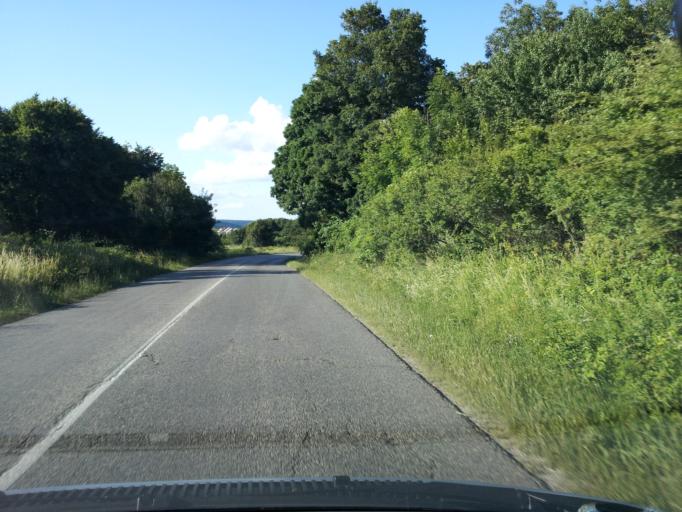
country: HU
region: Veszprem
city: Zirc
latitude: 47.2501
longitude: 17.8604
